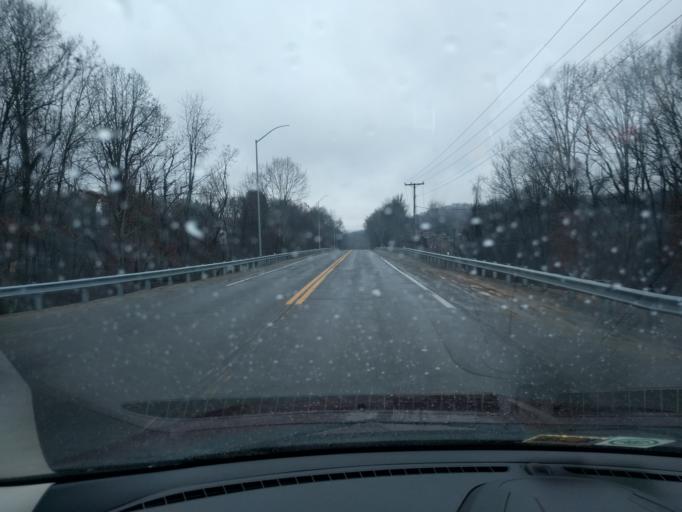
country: US
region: Virginia
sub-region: Pulaski County
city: Pulaski
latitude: 37.0349
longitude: -80.7347
